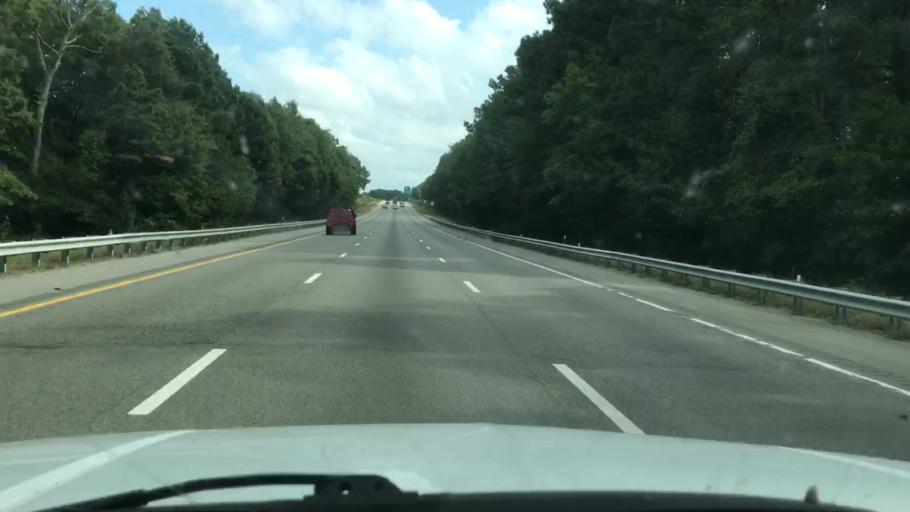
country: US
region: Virginia
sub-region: Henrico County
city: Short Pump
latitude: 37.6739
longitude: -77.5696
